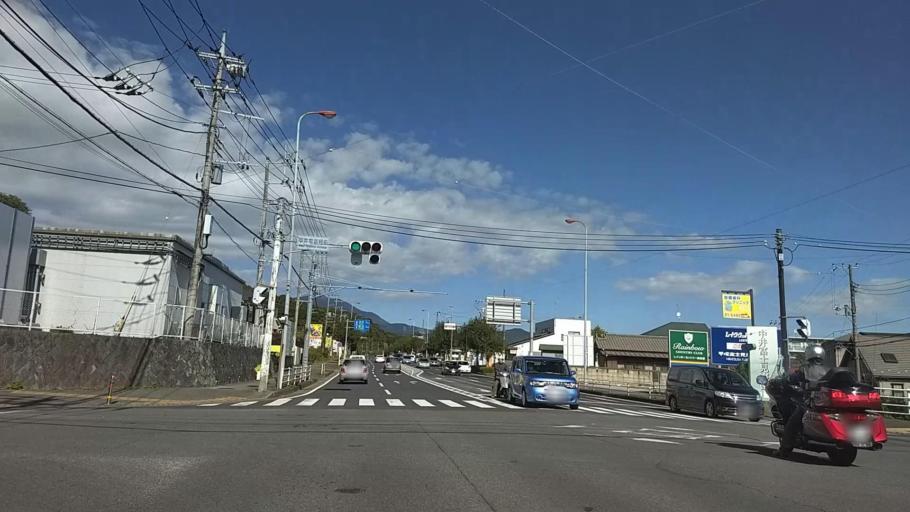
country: JP
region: Kanagawa
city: Hadano
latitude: 35.3384
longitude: 139.2299
